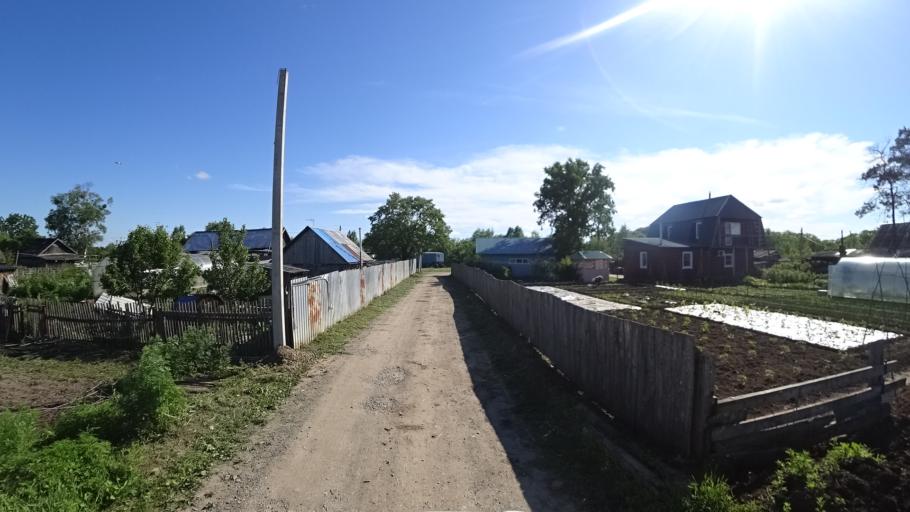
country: RU
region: Khabarovsk Krai
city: Khor
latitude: 47.8857
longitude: 135.0186
